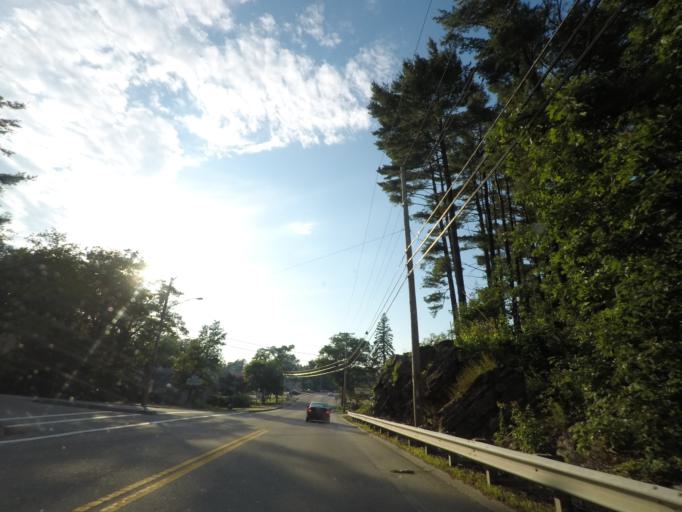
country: US
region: Massachusetts
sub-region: Worcester County
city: Sturbridge
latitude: 42.0951
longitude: -72.0705
